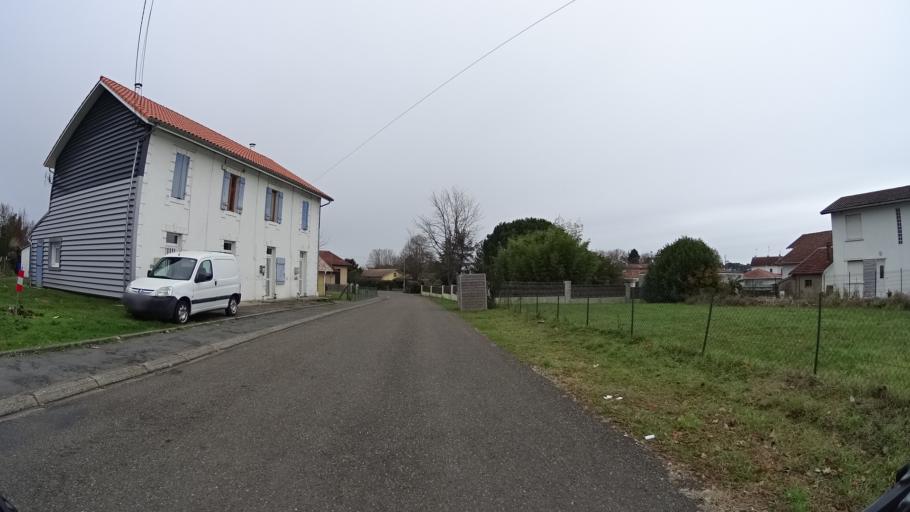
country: FR
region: Aquitaine
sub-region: Departement des Landes
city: Saint-Paul-les-Dax
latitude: 43.7310
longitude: -1.0503
